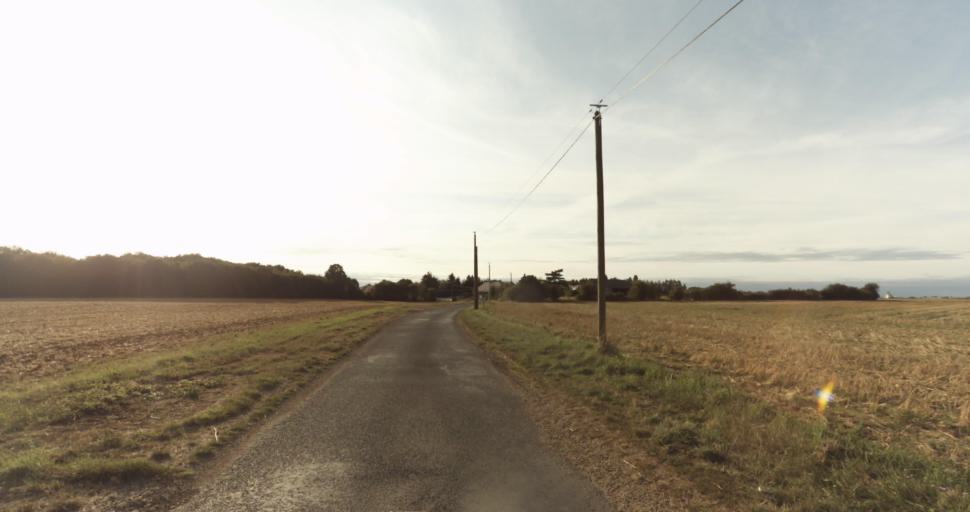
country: FR
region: Haute-Normandie
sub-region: Departement de l'Eure
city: Marcilly-sur-Eure
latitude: 48.8817
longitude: 1.2729
